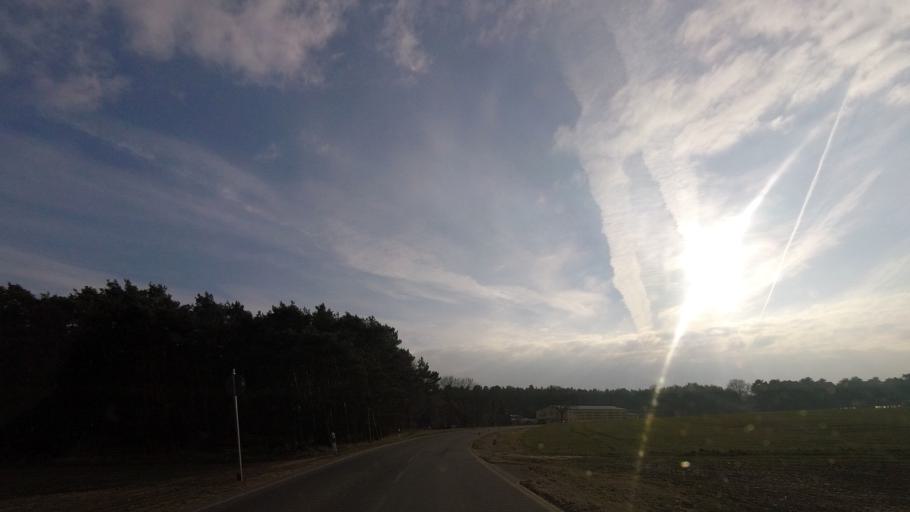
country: DE
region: Brandenburg
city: Belzig
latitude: 52.1354
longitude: 12.6442
